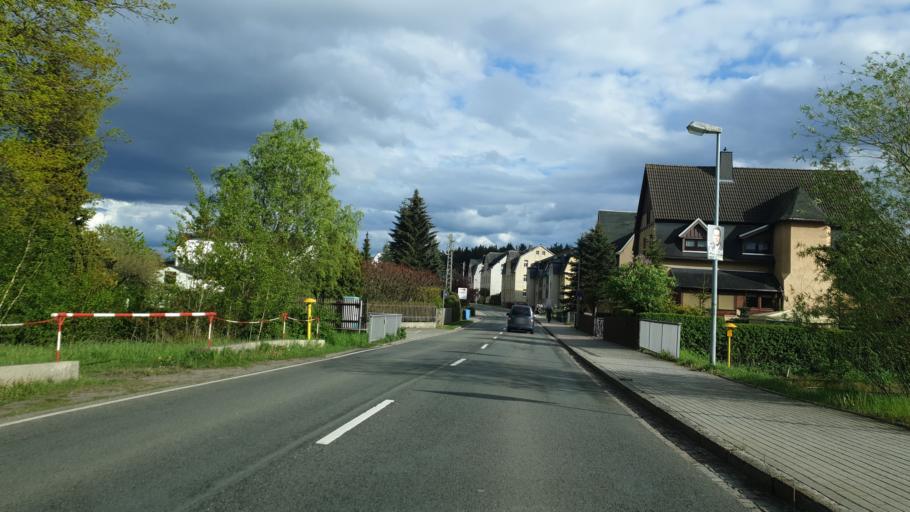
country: DE
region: Saxony
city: Oelsnitz
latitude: 50.7160
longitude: 12.7235
